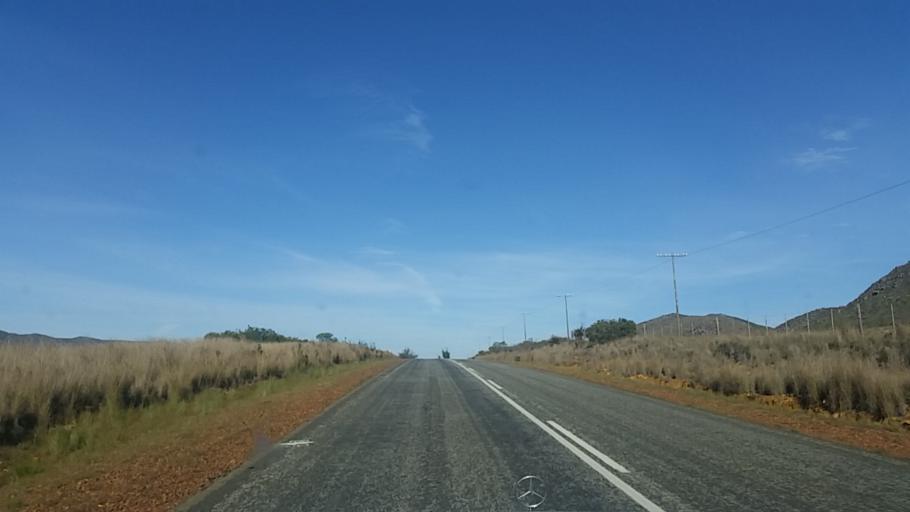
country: ZA
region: Western Cape
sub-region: Eden District Municipality
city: Knysna
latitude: -33.7725
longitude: 22.9393
